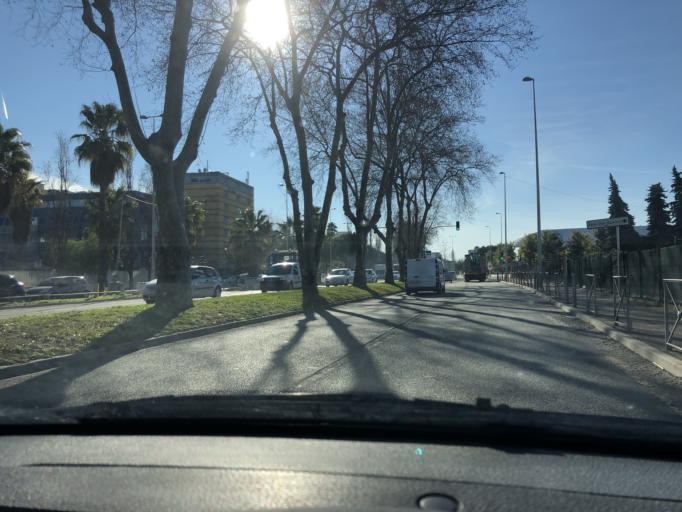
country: FR
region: Provence-Alpes-Cote d'Azur
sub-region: Departement des Alpes-Maritimes
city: Saint-Laurent-du-Var
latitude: 43.6817
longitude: 7.1988
